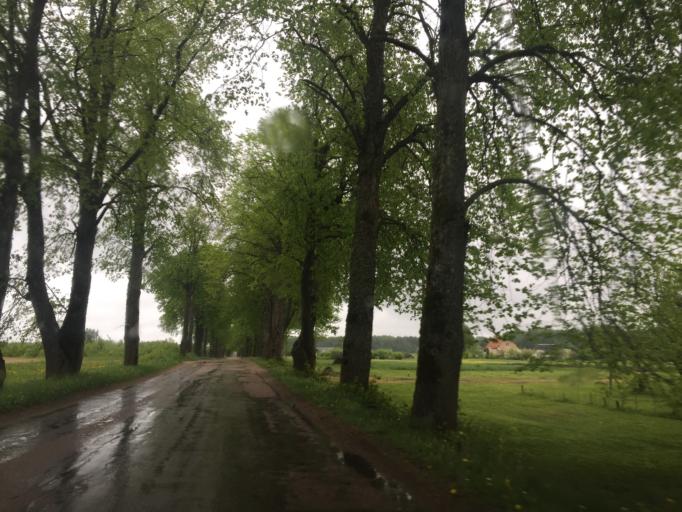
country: LV
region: Ogre
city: Jumprava
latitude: 56.6435
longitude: 24.9190
